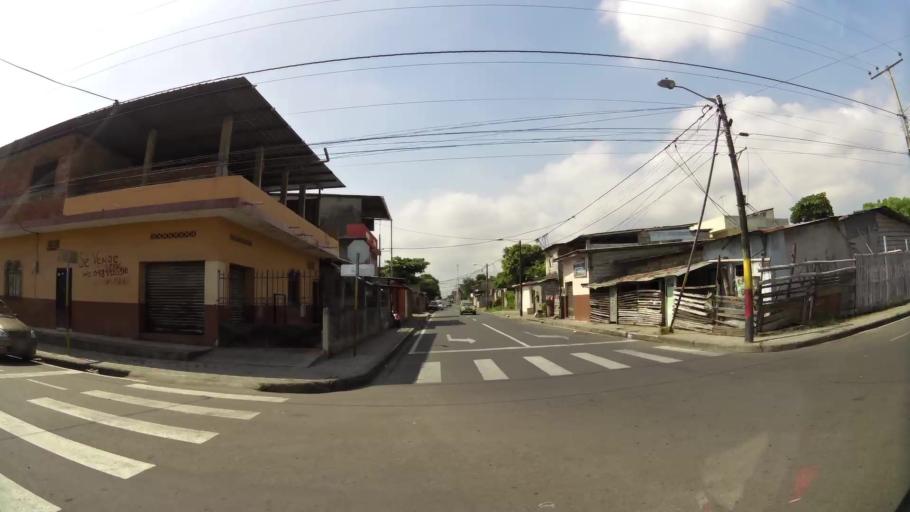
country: EC
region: Guayas
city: Eloy Alfaro
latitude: -2.1546
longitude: -79.8401
